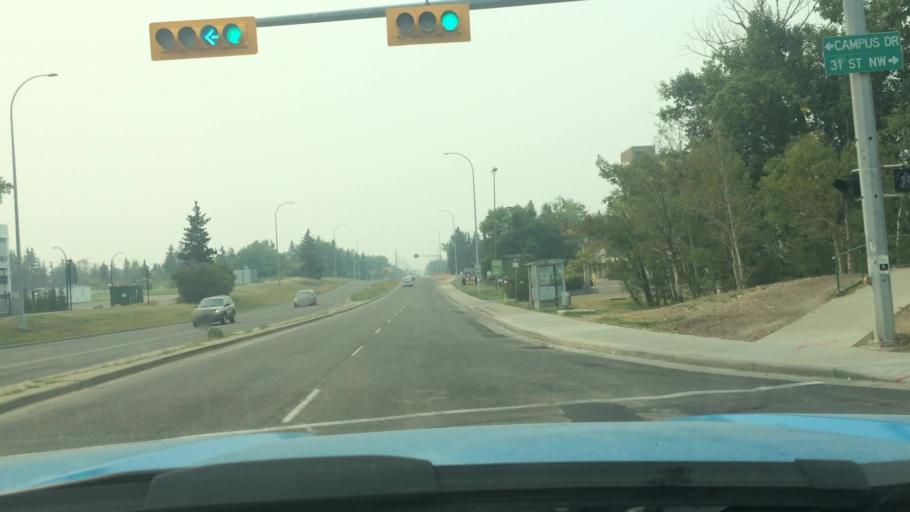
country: CA
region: Alberta
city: Calgary
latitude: 51.0816
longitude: -114.1307
